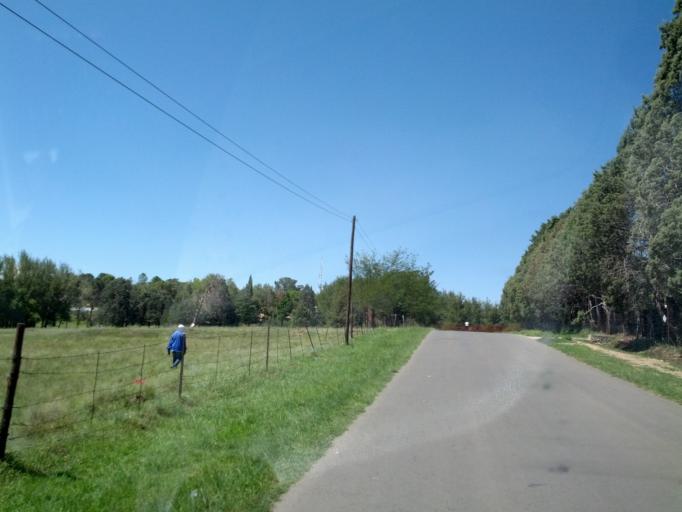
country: LS
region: Maseru
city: Maseru
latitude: -29.3115
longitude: 27.4719
